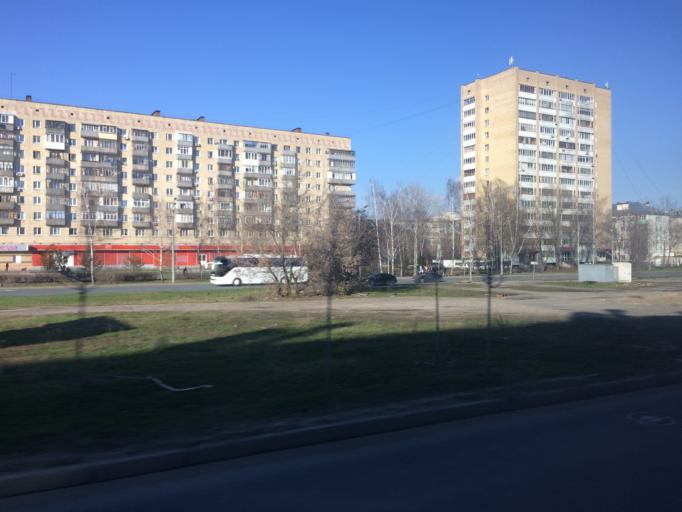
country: RU
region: Tatarstan
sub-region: Gorod Kazan'
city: Kazan
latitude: 55.8199
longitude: 49.0525
